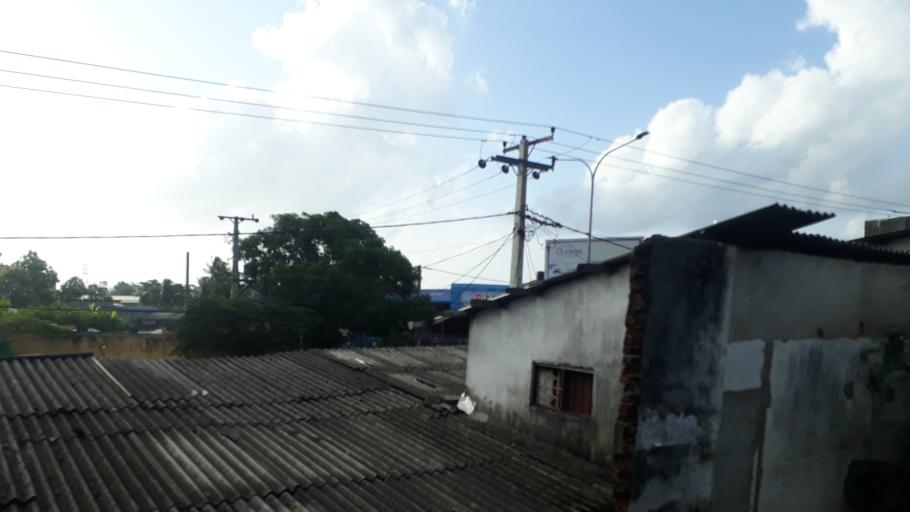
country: LK
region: Western
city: Peliyagoda
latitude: 6.9577
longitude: 79.8901
